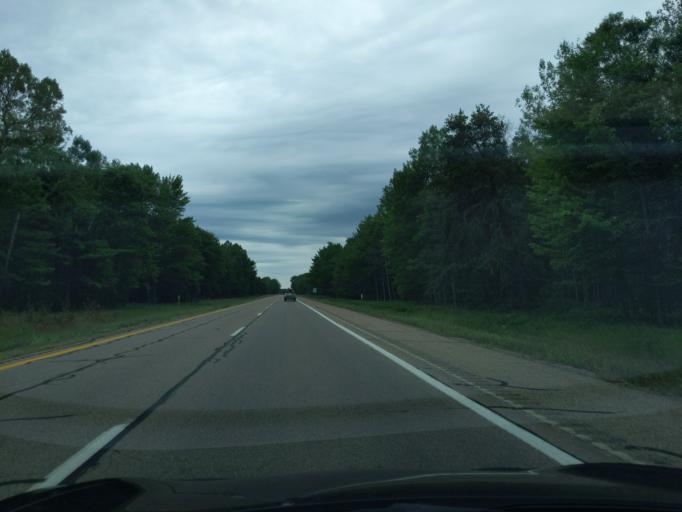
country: US
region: Michigan
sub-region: Roscommon County
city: Houghton Lake
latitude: 44.2541
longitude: -84.8041
